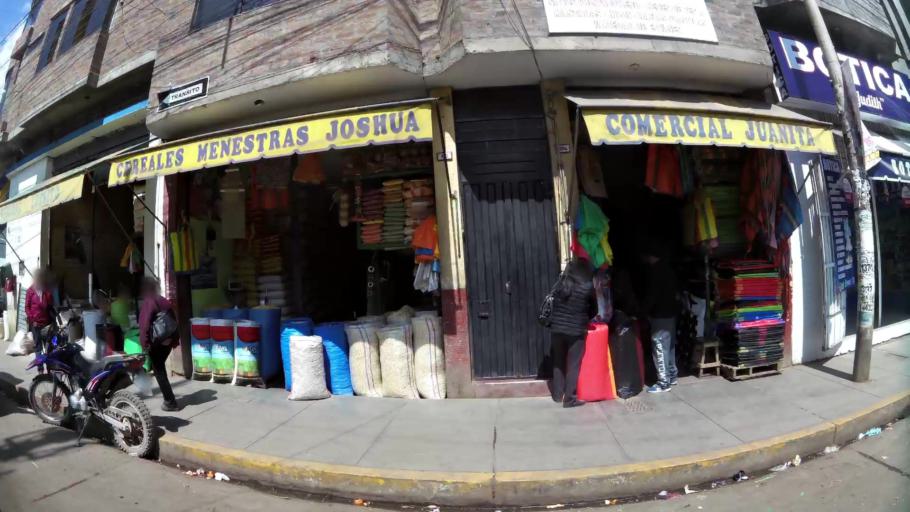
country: PE
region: Junin
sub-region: Provincia de Huancayo
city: Huancayo
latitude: -12.0673
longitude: -75.2022
